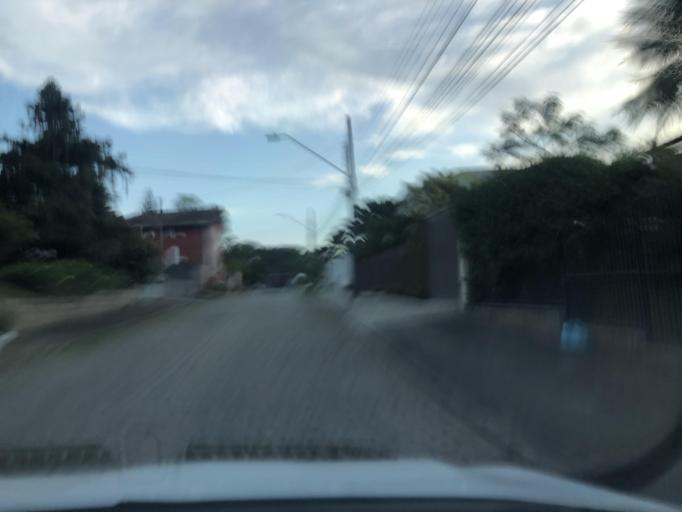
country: BR
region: Santa Catarina
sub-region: Joinville
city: Joinville
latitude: -26.2947
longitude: -48.8633
